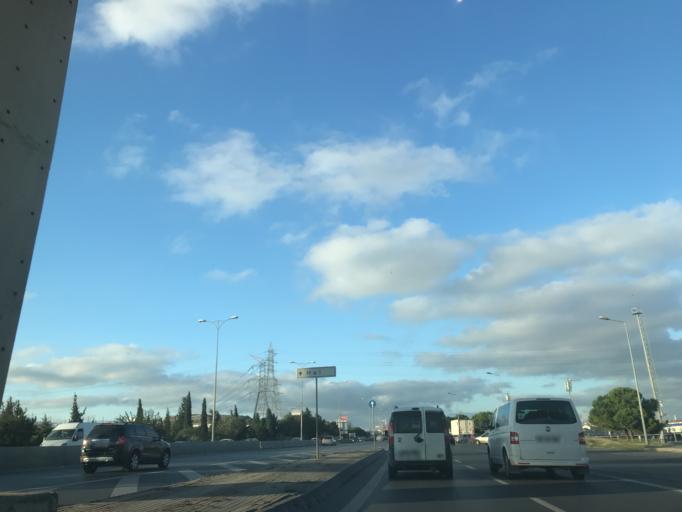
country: TR
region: Istanbul
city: Esenler
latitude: 41.0493
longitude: 28.8854
